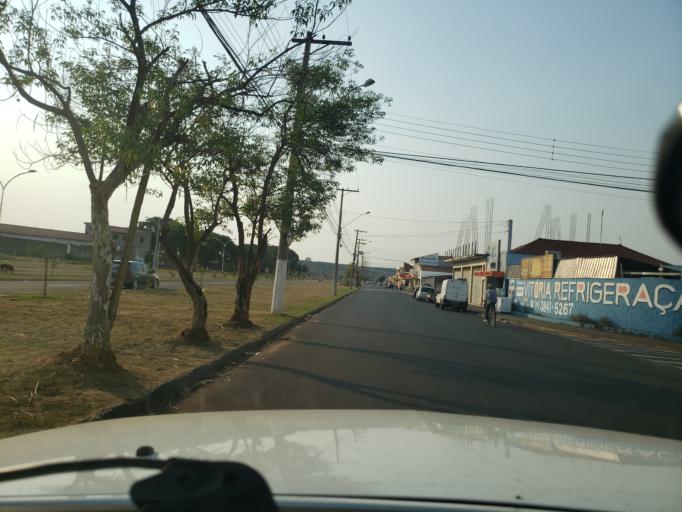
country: BR
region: Sao Paulo
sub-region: Moji-Guacu
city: Mogi-Gaucu
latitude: -22.3352
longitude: -46.9453
